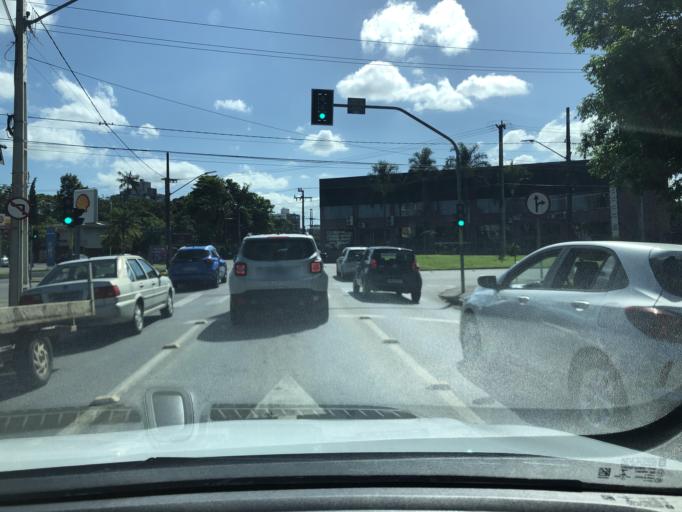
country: BR
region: Santa Catarina
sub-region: Joinville
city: Joinville
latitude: -26.2719
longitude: -48.8507
